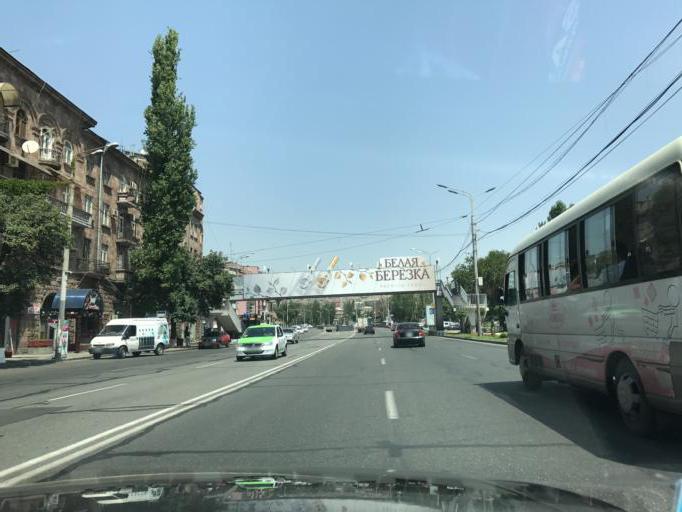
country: AM
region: Yerevan
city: Yerevan
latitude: 40.1775
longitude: 44.5226
